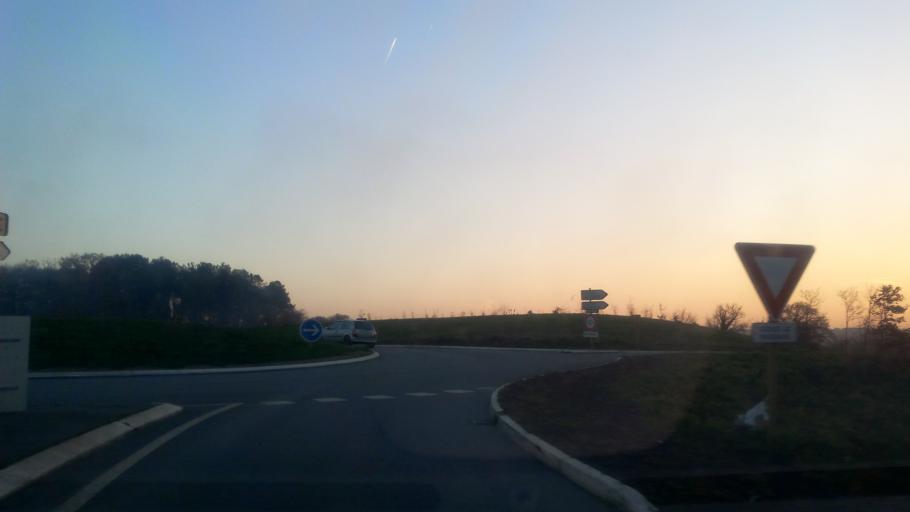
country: FR
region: Brittany
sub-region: Departement d'Ille-et-Vilaine
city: Bains-sur-Oust
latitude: 47.6911
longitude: -2.0571
